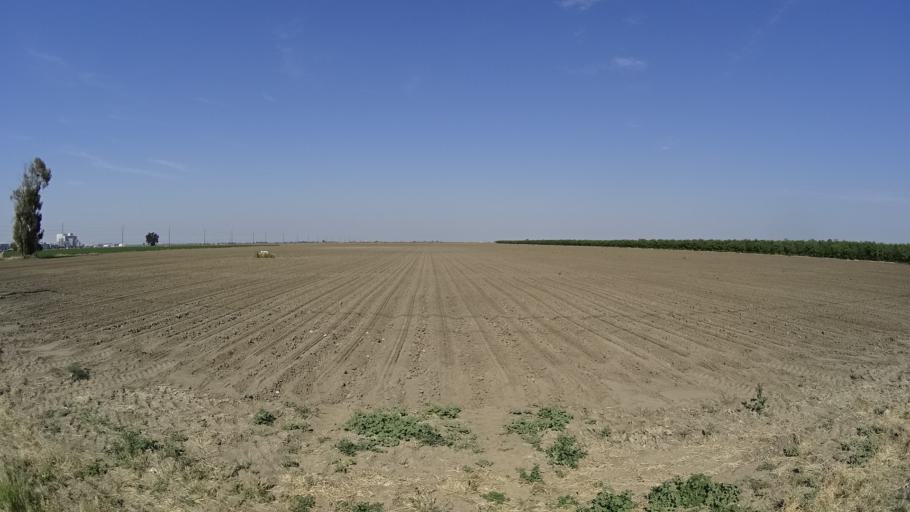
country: US
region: California
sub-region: Kings County
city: Lemoore
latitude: 36.3085
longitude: -119.8087
